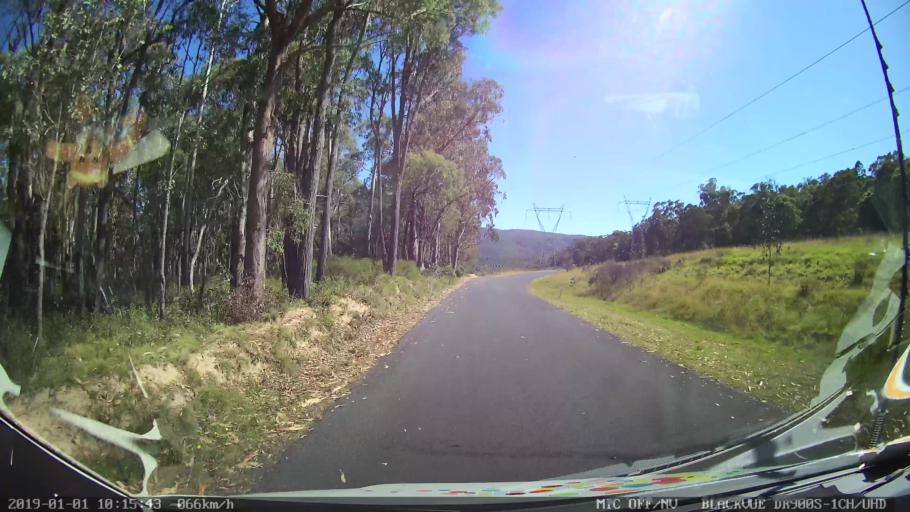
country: AU
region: New South Wales
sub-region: Snowy River
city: Jindabyne
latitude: -36.0989
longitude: 148.1621
